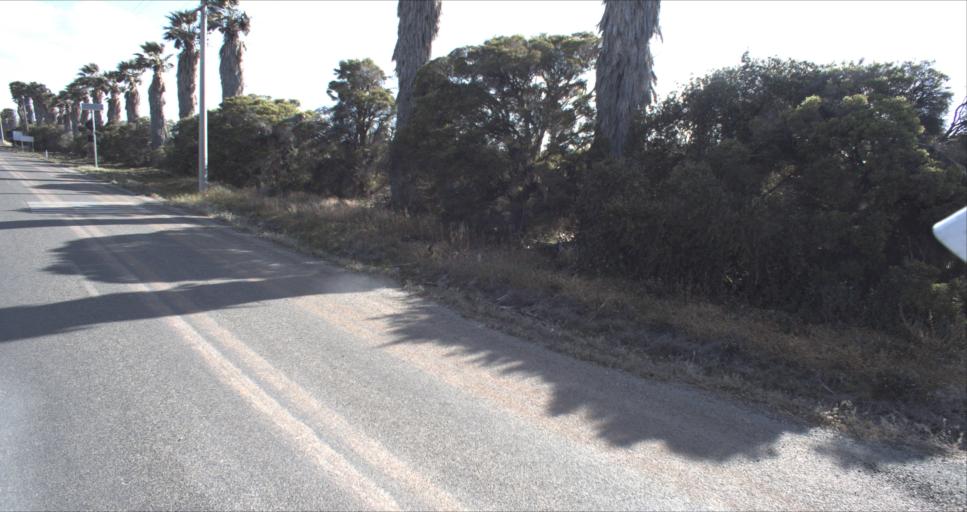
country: AU
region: New South Wales
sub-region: Leeton
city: Leeton
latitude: -34.5213
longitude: 146.2832
